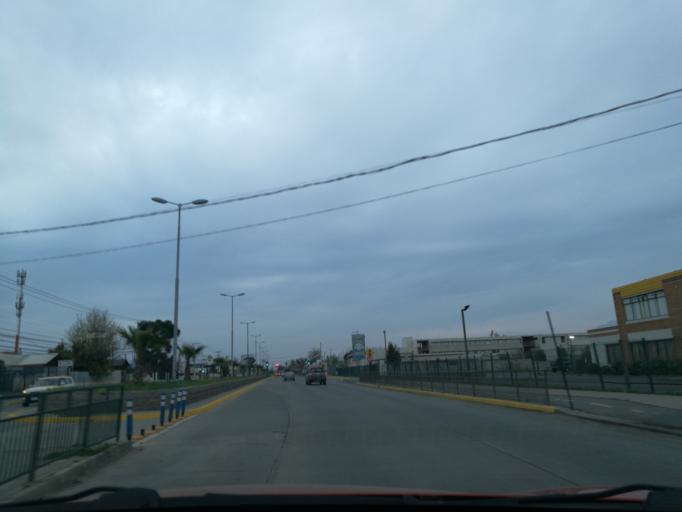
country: CL
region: O'Higgins
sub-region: Provincia de Cachapoal
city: Machali
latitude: -34.1737
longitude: -70.6892
